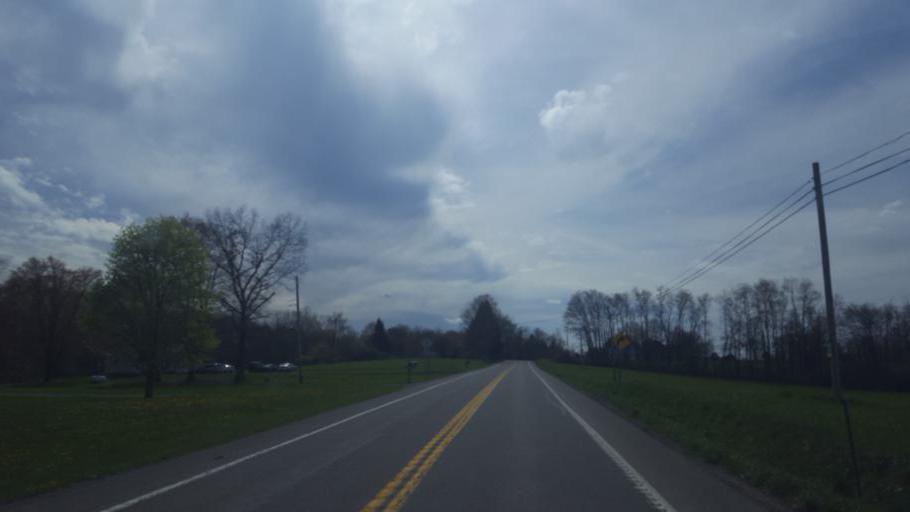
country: US
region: Pennsylvania
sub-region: Mercer County
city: Stoneboro
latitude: 41.3482
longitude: -80.0428
